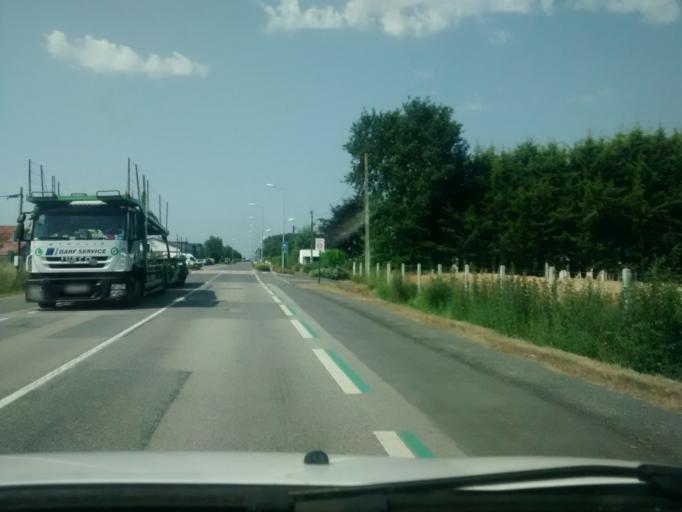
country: FR
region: Brittany
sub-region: Departement d'Ille-et-Vilaine
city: Cesson-Sevigne
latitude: 48.1419
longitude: -1.6140
